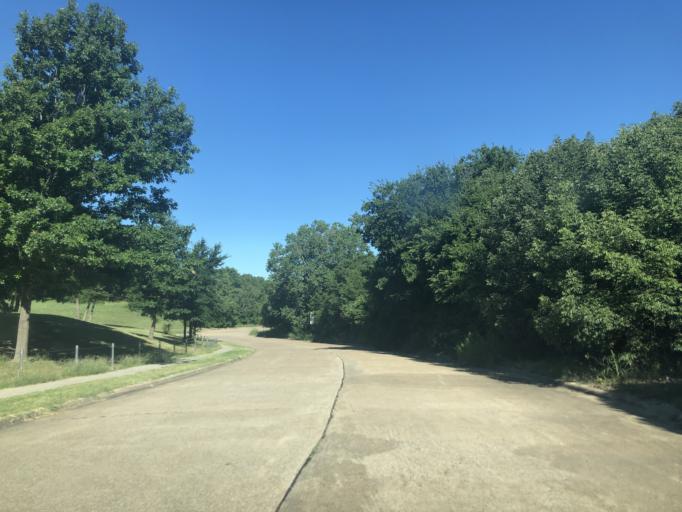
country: US
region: Texas
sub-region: Dallas County
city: Duncanville
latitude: 32.6668
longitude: -96.9292
